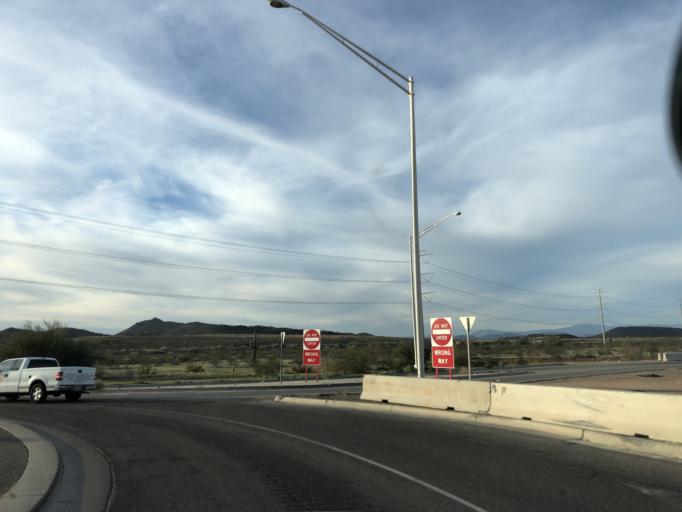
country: US
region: Arizona
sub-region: Maricopa County
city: Anthem
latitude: 33.7132
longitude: -112.1201
